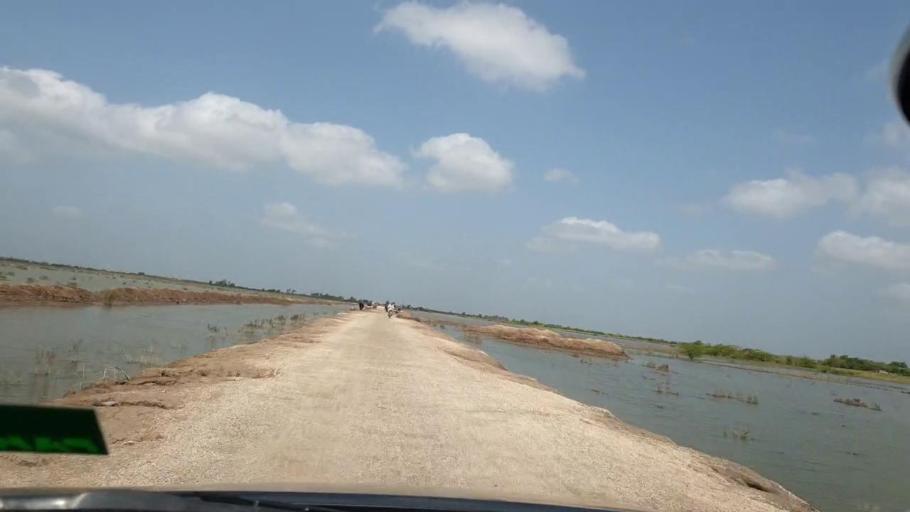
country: PK
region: Sindh
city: Kadhan
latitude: 24.5937
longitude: 69.1327
